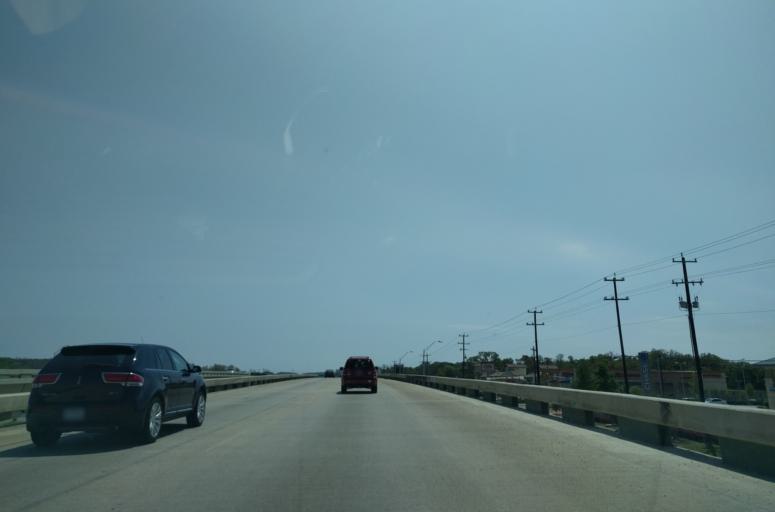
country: US
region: Texas
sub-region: Bexar County
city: Cross Mountain
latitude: 29.6494
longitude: -98.6234
